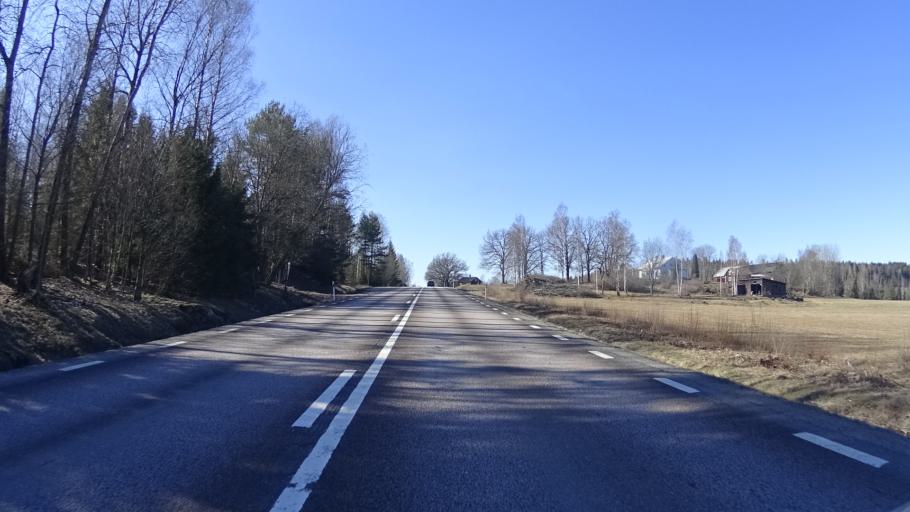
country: SE
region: Vaermland
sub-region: Karlstads Kommun
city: Edsvalla
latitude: 59.5274
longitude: 13.1291
